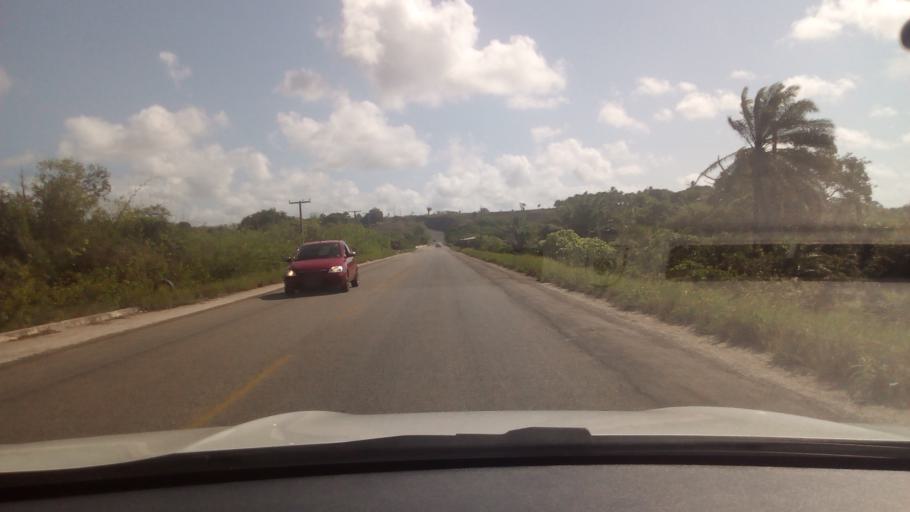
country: BR
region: Paraiba
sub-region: Conde
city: Conde
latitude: -7.2325
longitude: -34.8423
